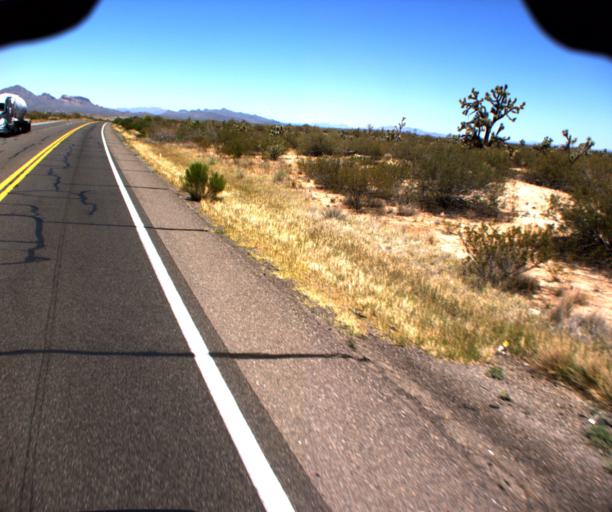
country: US
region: Arizona
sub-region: Yavapai County
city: Congress
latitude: 34.1859
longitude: -113.0459
